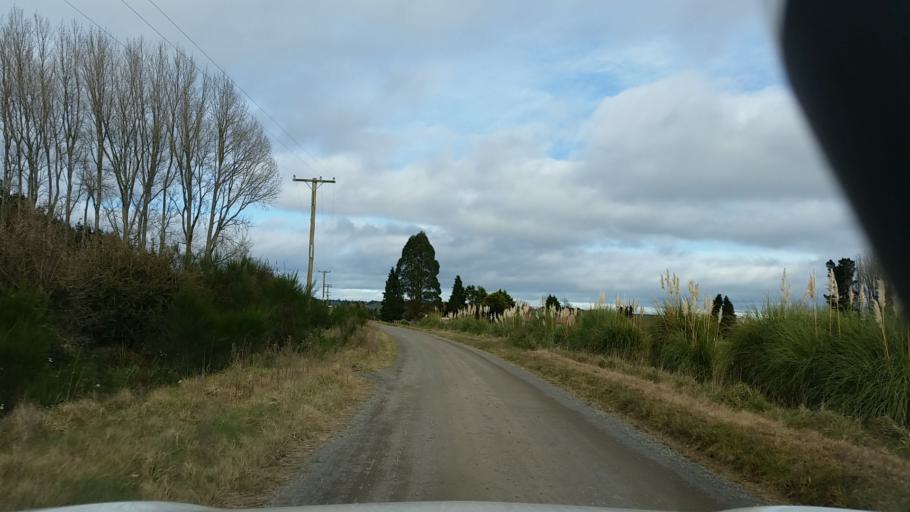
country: NZ
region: Bay of Plenty
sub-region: Whakatane District
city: Murupara
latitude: -38.2858
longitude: 176.5489
